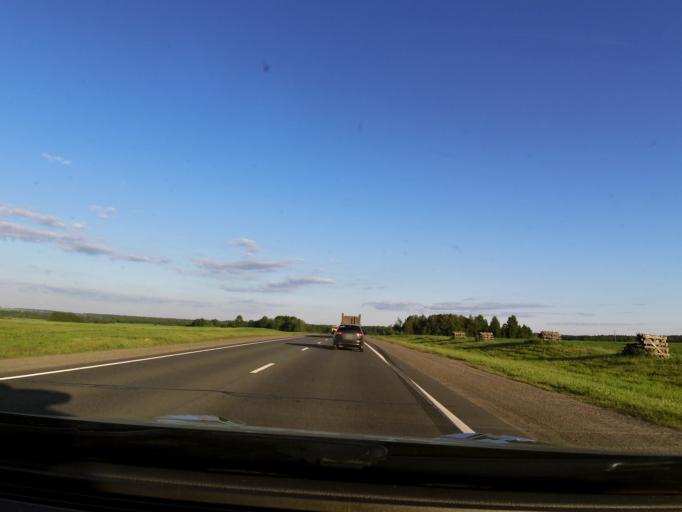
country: RU
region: Vologda
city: Vologda
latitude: 59.1472
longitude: 39.9411
